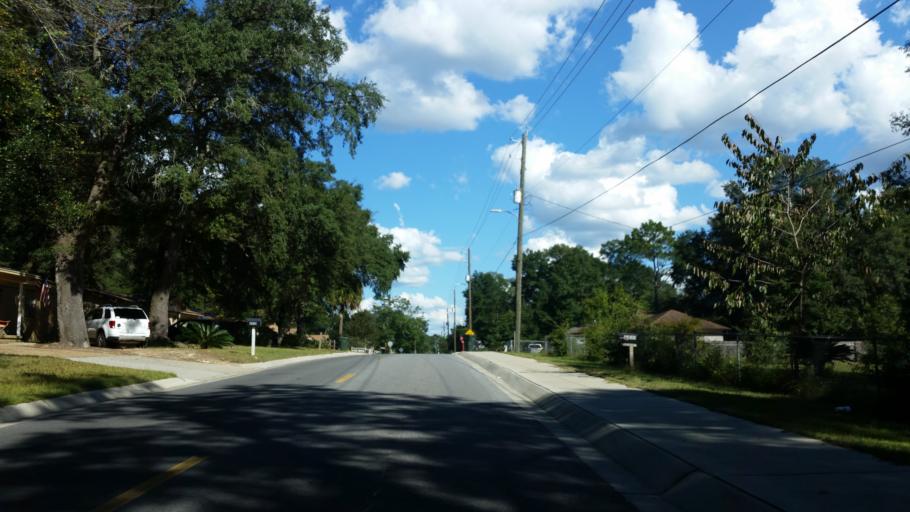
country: US
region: Florida
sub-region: Santa Rosa County
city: Milton
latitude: 30.6382
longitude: -87.0544
